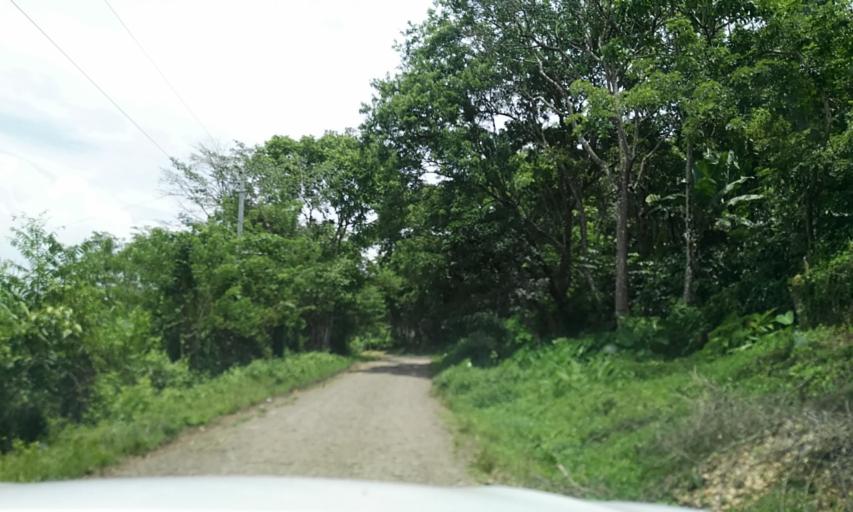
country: NI
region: Matagalpa
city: San Ramon
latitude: 12.9879
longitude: -85.8529
